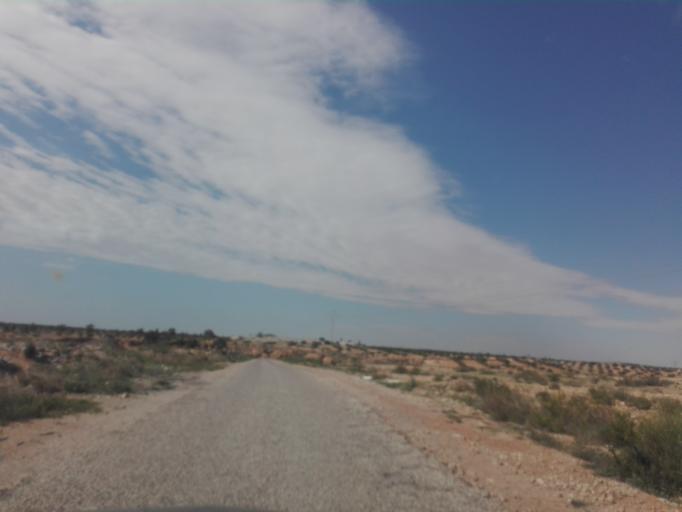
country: TN
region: Safaqis
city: Sfax
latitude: 34.6896
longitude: 10.5628
